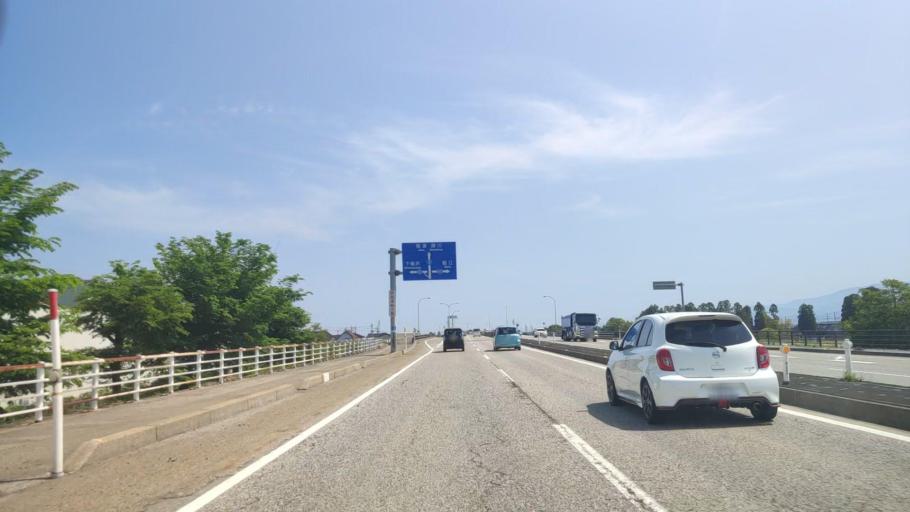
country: JP
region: Toyama
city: Namerikawa
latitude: 36.7382
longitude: 137.3398
